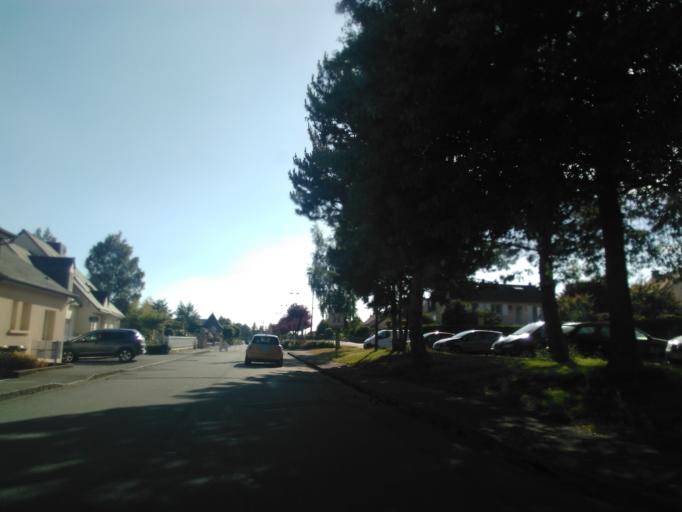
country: FR
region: Brittany
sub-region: Departement d'Ille-et-Vilaine
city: Pleumeleuc
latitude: 48.1842
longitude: -1.9212
